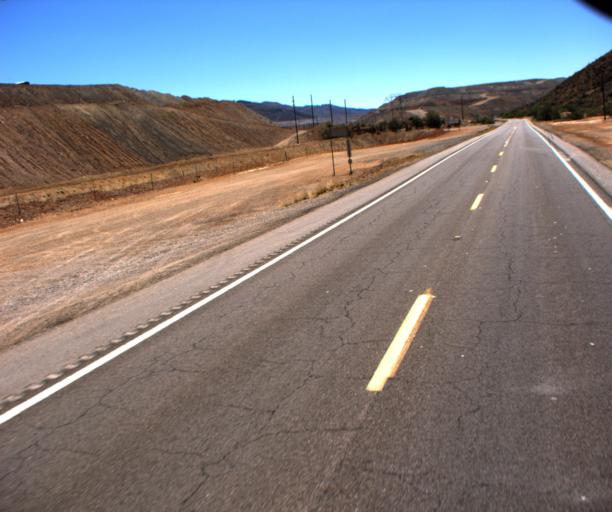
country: US
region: Arizona
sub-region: Pinal County
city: Kearny
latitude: 33.1674
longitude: -111.0071
